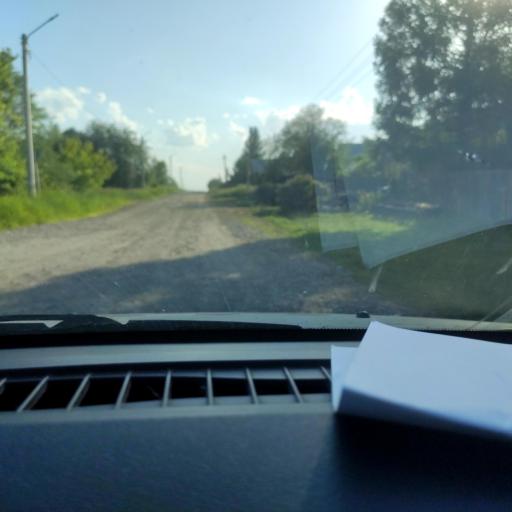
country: RU
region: Perm
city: Krasnokamsk
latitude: 58.1379
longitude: 55.6796
